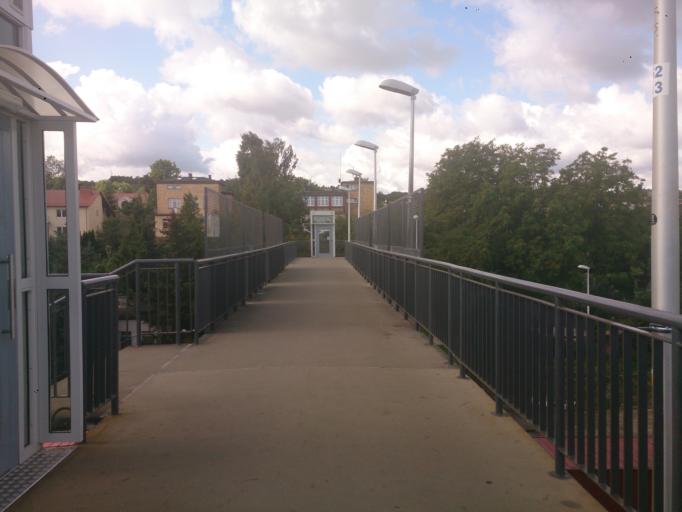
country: PL
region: Pomeranian Voivodeship
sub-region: Sopot
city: Sopot
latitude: 54.4776
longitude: 18.5479
